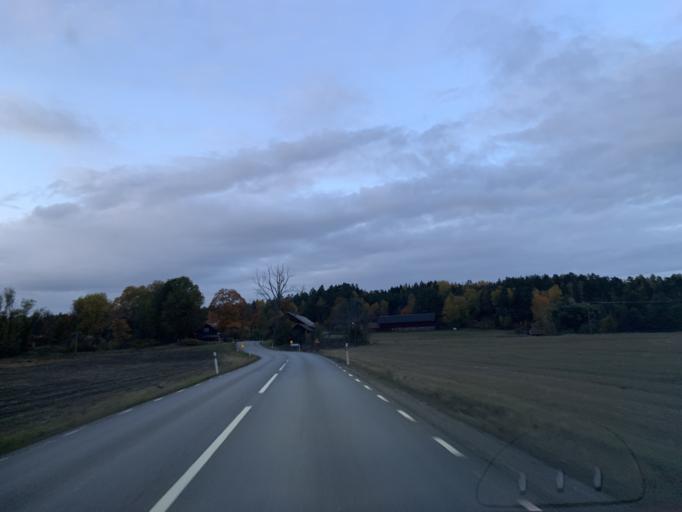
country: SE
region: Stockholm
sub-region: Botkyrka Kommun
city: Varsta
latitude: 59.0597
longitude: 17.8057
